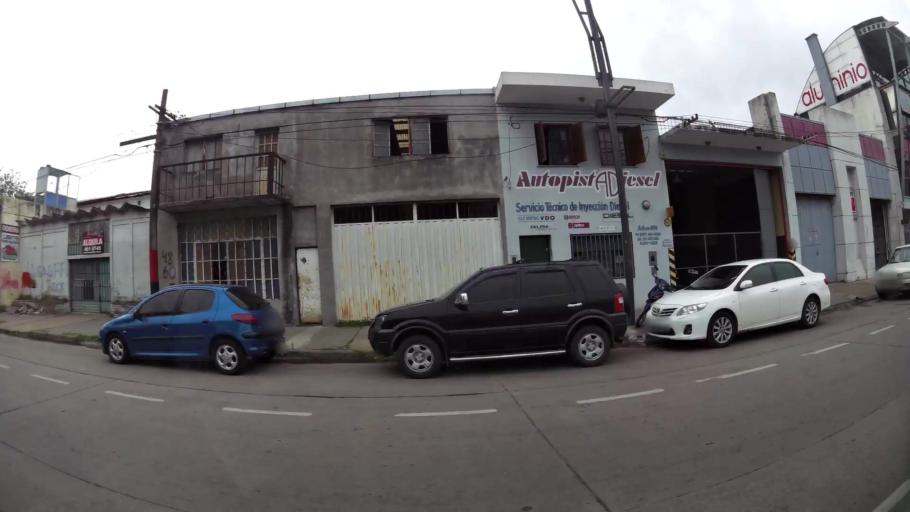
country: AR
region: Santa Fe
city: Gobernador Galvez
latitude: -32.9941
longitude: -60.6655
